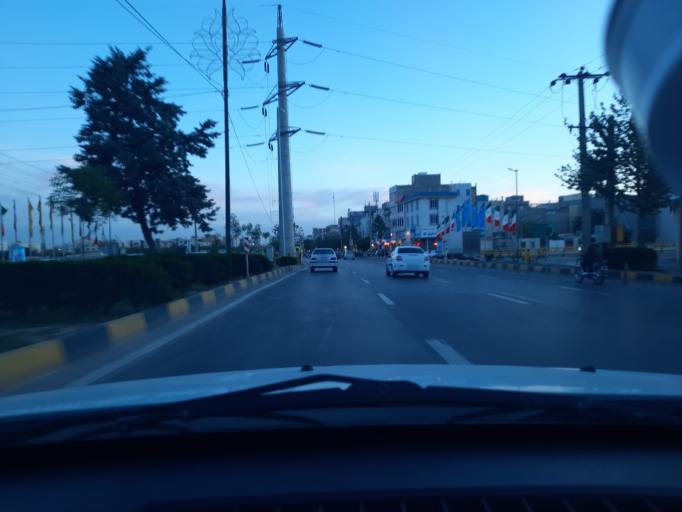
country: IR
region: Qazvin
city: Qazvin
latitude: 36.3058
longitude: 50.0115
